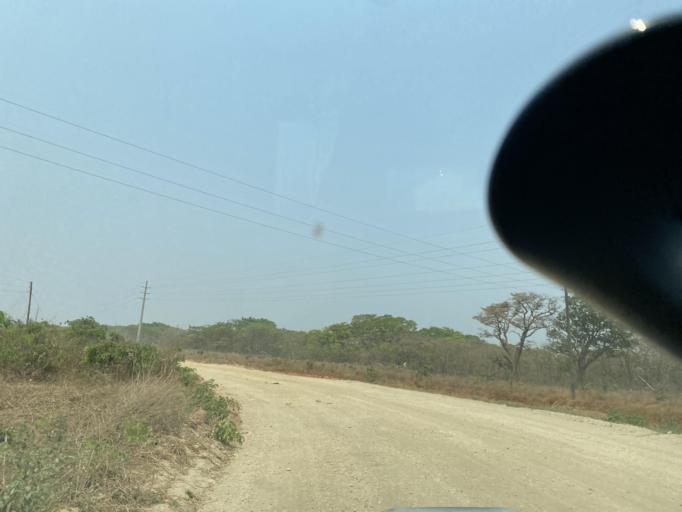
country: ZM
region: Lusaka
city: Lusaka
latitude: -15.5325
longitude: 28.3426
